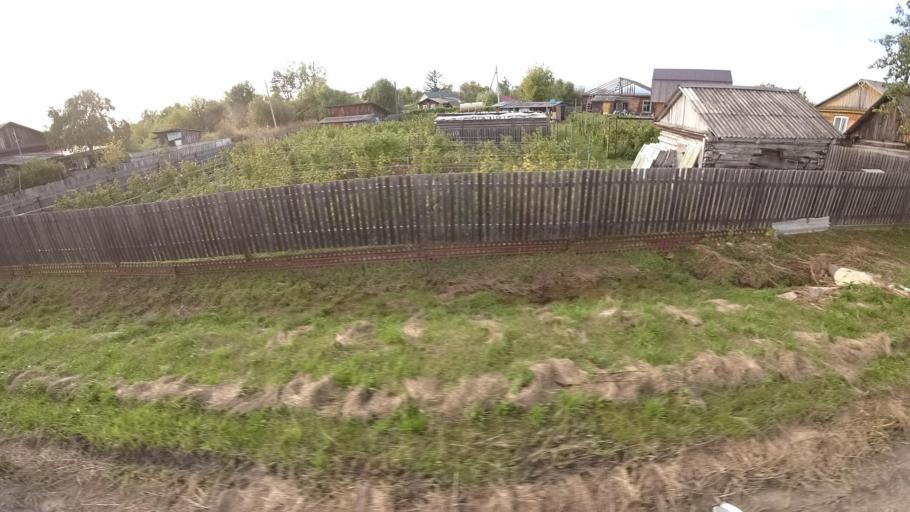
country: RU
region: Primorskiy
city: Dostoyevka
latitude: 44.2875
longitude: 133.4295
